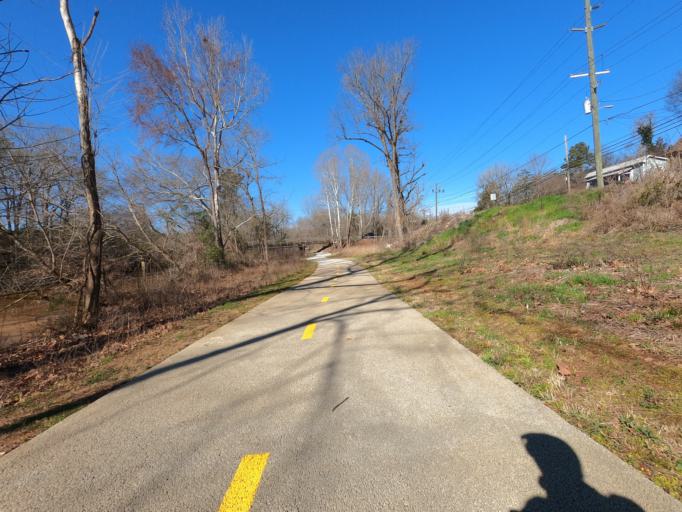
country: US
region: Georgia
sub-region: Clarke County
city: Athens
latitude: 33.9697
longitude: -83.3764
